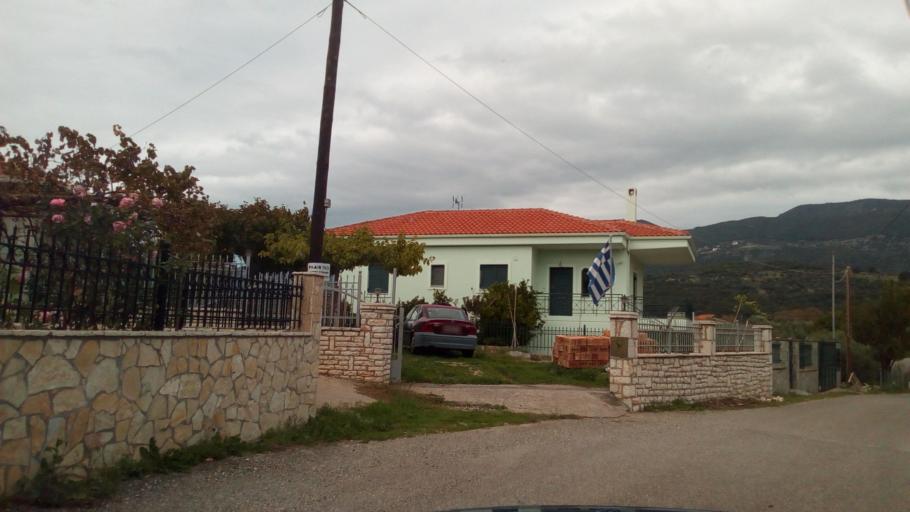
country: GR
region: West Greece
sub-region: Nomos Achaias
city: Kamarai
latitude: 38.4148
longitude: 21.9528
